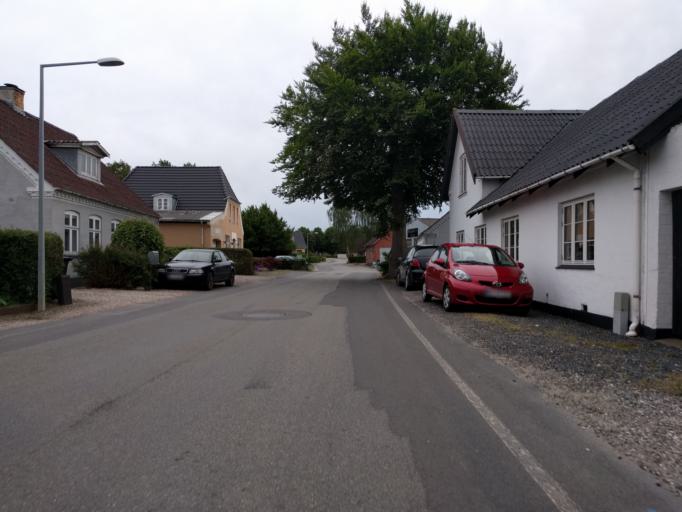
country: DK
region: South Denmark
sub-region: Kerteminde Kommune
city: Langeskov
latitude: 55.3987
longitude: 10.6099
